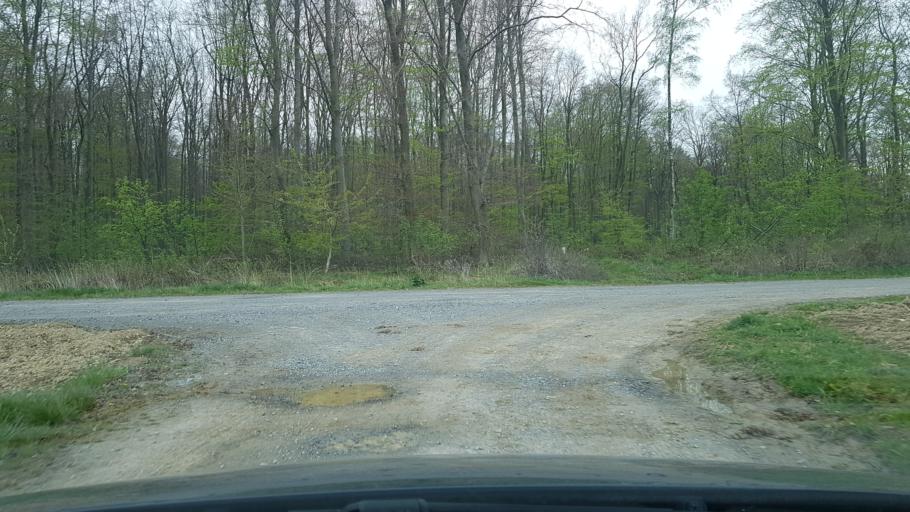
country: DE
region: North Rhine-Westphalia
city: Lichtenau
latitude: 51.6273
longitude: 8.8201
